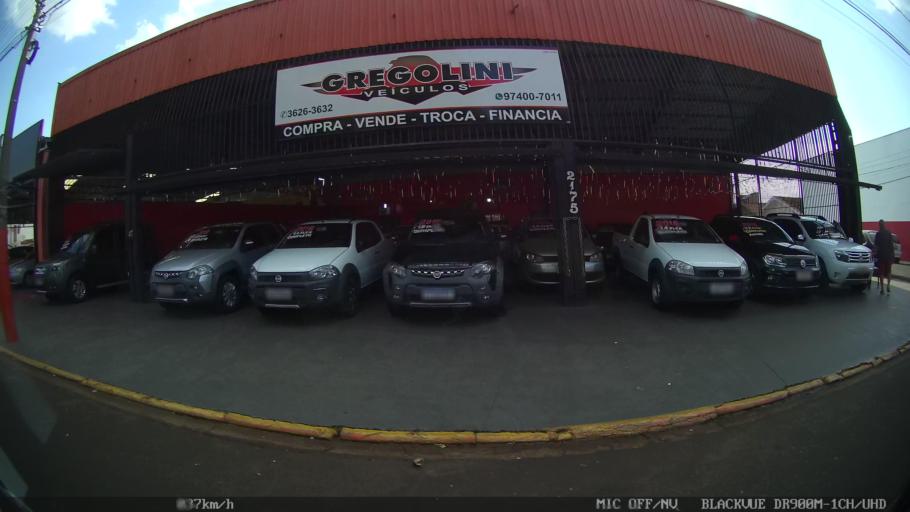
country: BR
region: Sao Paulo
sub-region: Ribeirao Preto
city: Ribeirao Preto
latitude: -21.1496
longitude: -47.8038
